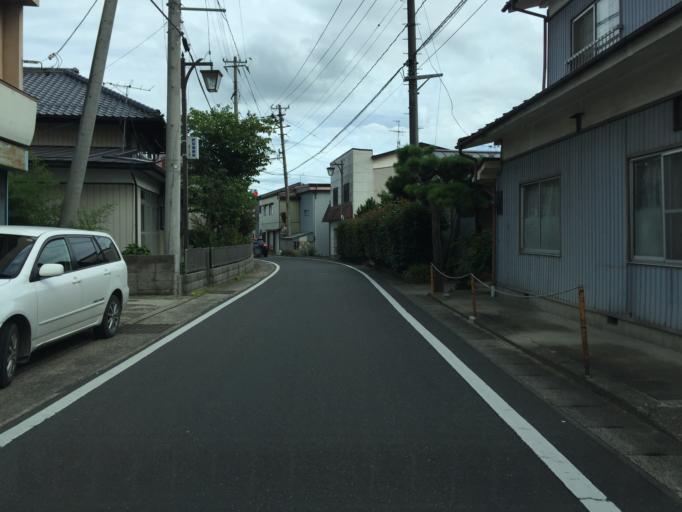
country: JP
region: Fukushima
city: Motomiya
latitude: 37.5308
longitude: 140.3692
